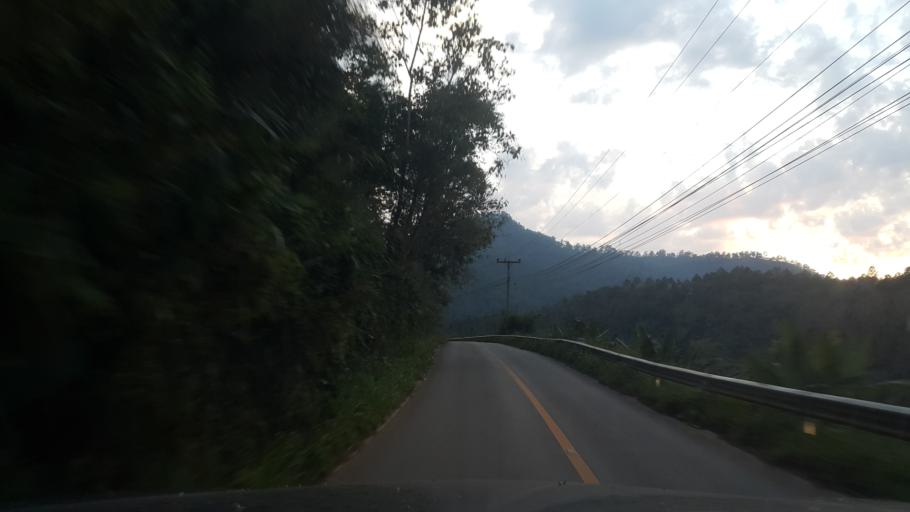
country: TH
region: Chiang Mai
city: Samoeng
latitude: 18.9454
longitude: 98.6738
